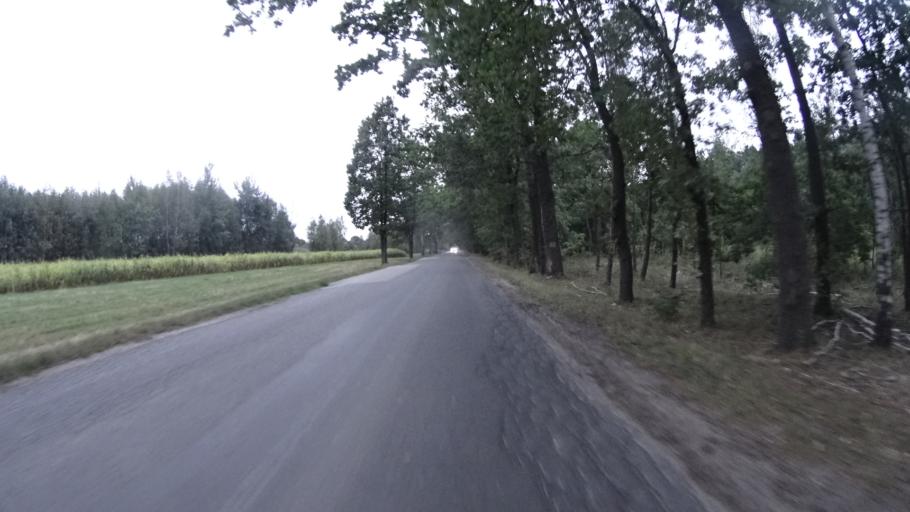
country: PL
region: Masovian Voivodeship
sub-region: Powiat warszawski zachodni
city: Stare Babice
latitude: 52.2742
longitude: 20.8348
